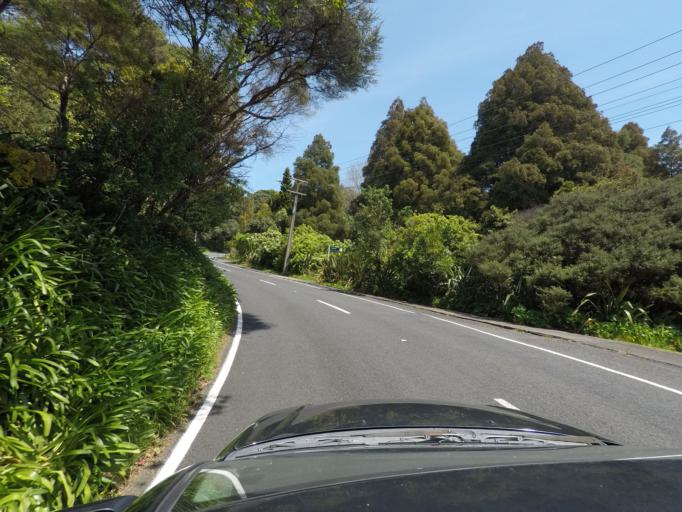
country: NZ
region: Auckland
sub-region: Auckland
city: Titirangi
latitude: -36.9692
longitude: 174.6363
